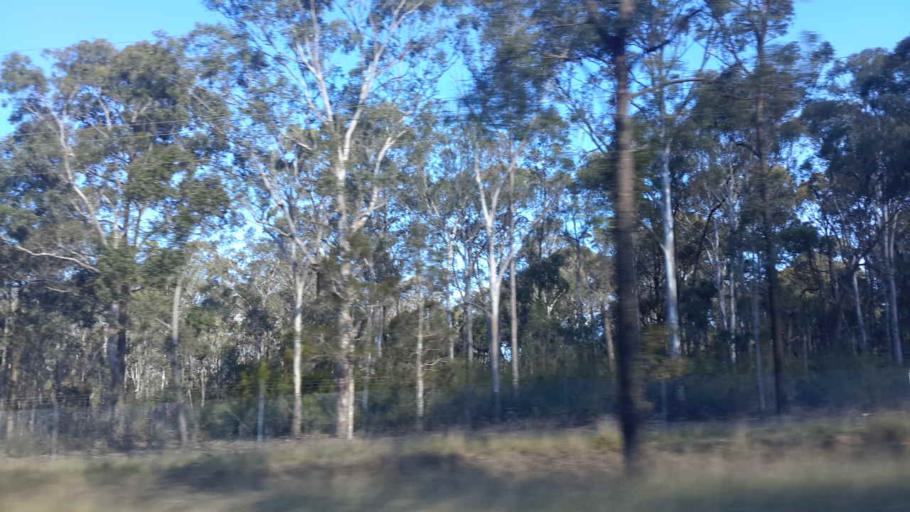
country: AU
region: New South Wales
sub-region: Hawkesbury
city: South Windsor
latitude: -33.6452
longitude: 150.7821
